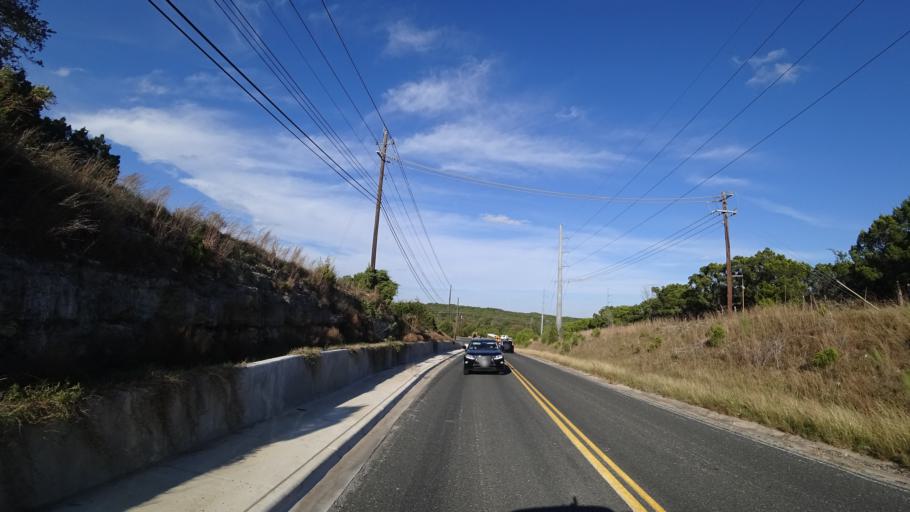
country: US
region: Texas
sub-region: Travis County
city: Barton Creek
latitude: 30.2485
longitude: -97.8538
